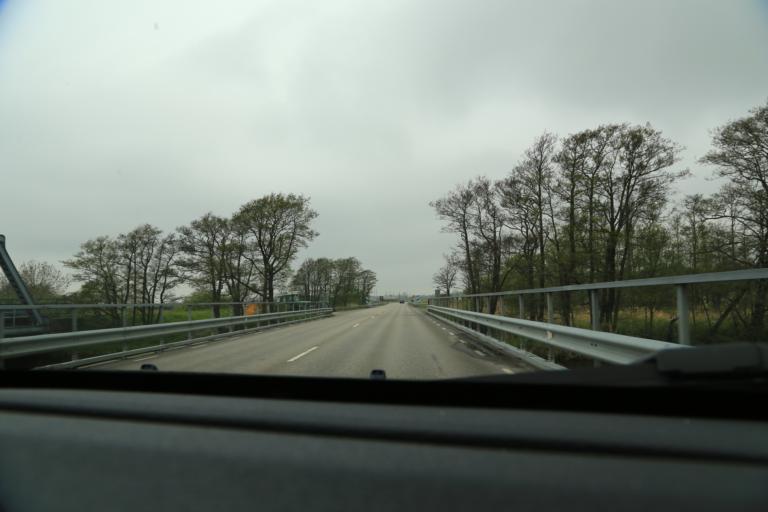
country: SE
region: Halland
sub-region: Kungsbacka Kommun
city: Frillesas
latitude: 57.2272
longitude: 12.2143
